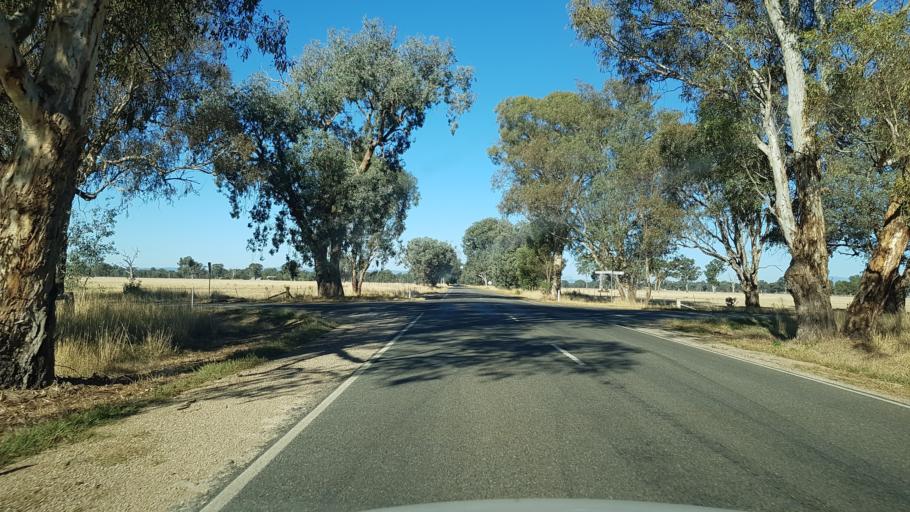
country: AU
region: Victoria
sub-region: Wangaratta
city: Wangaratta
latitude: -36.4357
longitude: 146.3232
